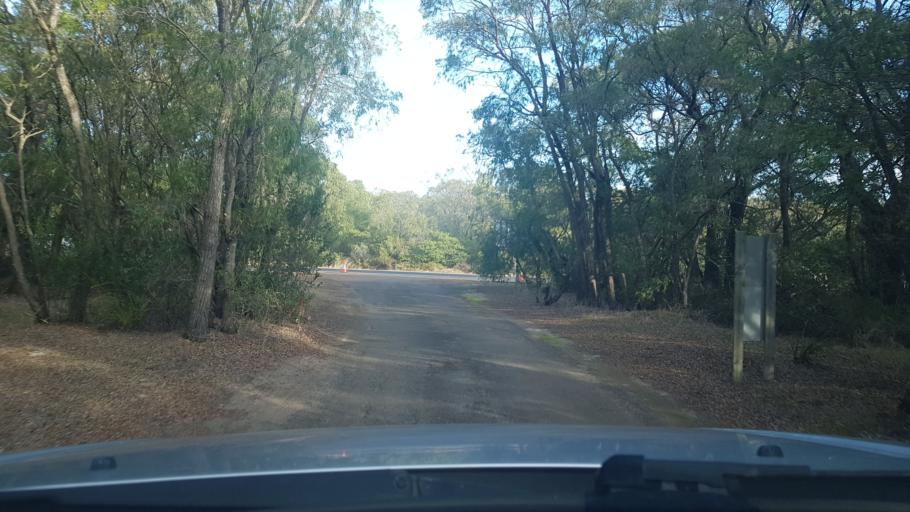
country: AU
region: Western Australia
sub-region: Busselton
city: Vasse
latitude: -33.6577
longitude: 115.2367
